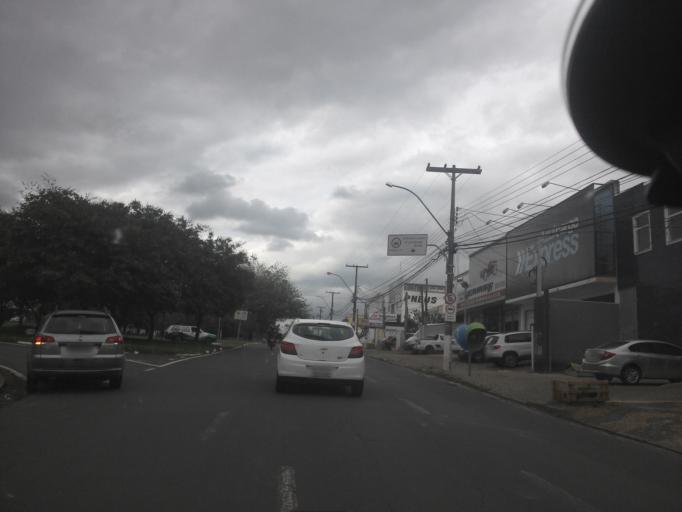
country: BR
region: Sao Paulo
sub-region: Campinas
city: Campinas
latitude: -22.8762
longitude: -47.0673
